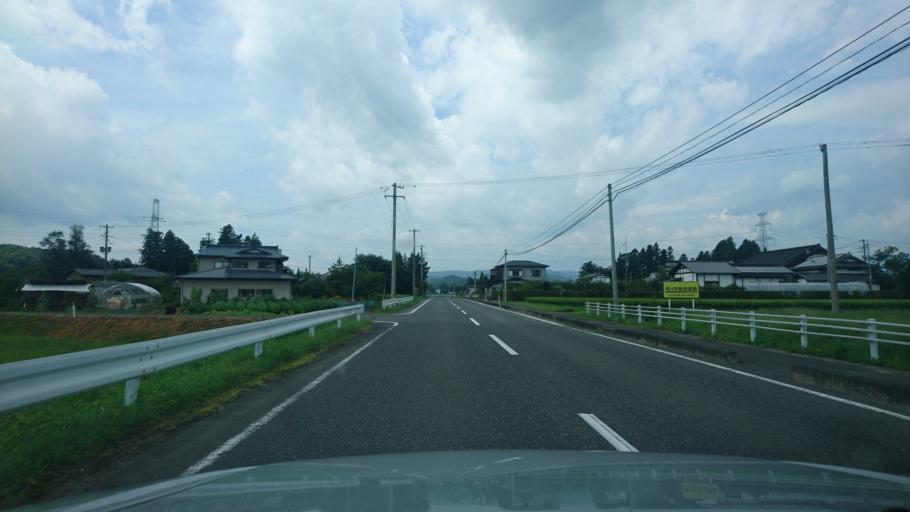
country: JP
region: Iwate
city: Ichinoseki
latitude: 38.8032
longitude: 140.9660
